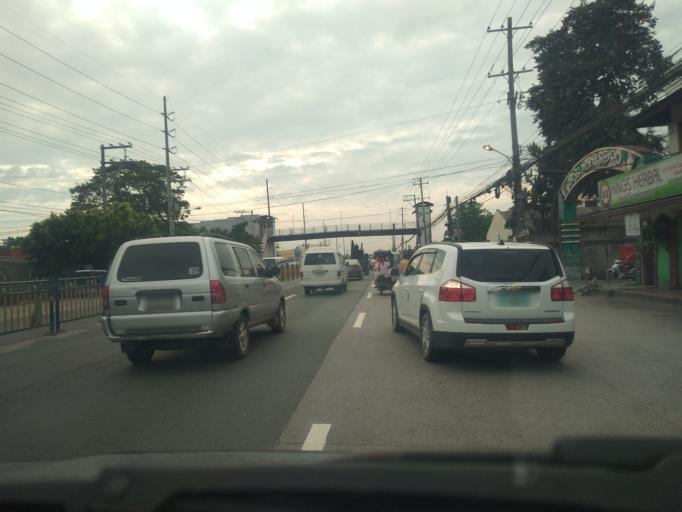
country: PH
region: Central Luzon
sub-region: Province of Pampanga
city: Magliman
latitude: 15.0570
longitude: 120.6587
